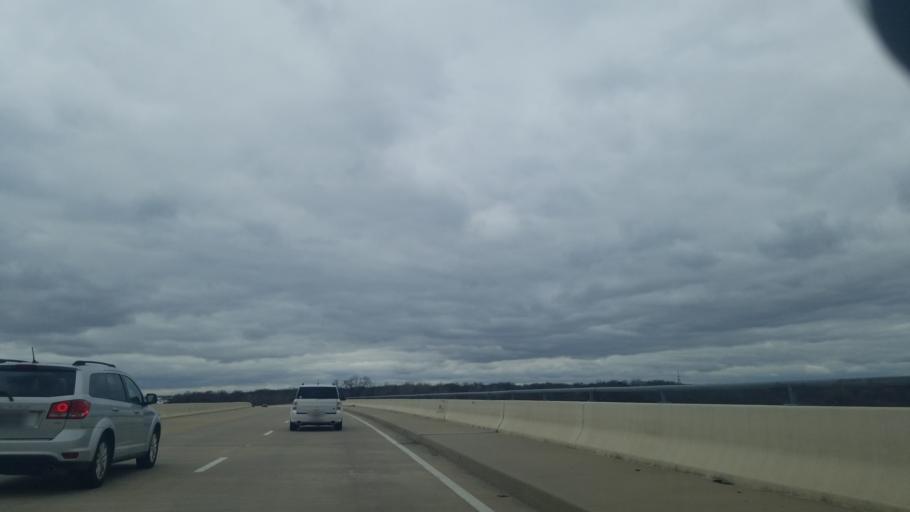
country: US
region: Texas
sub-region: Denton County
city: Copper Canyon
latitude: 33.1207
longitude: -97.0810
